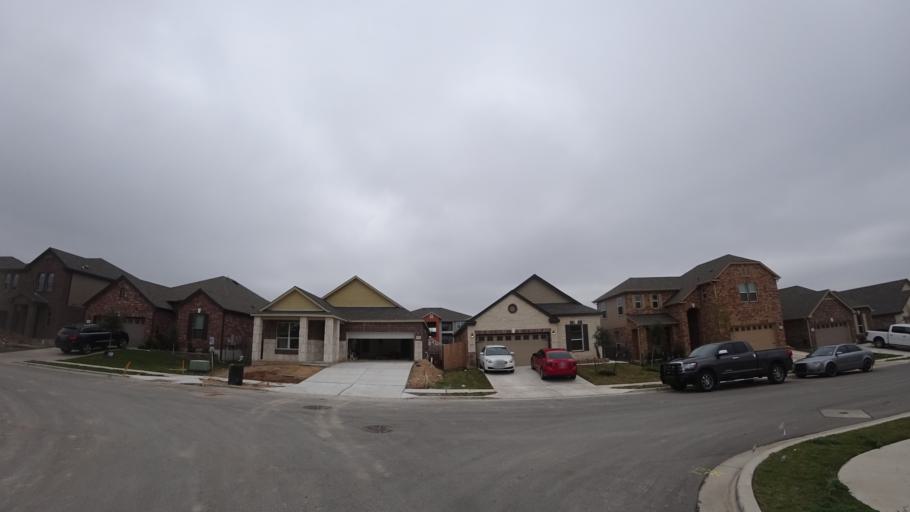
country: US
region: Texas
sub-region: Travis County
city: Pflugerville
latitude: 30.3919
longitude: -97.6492
